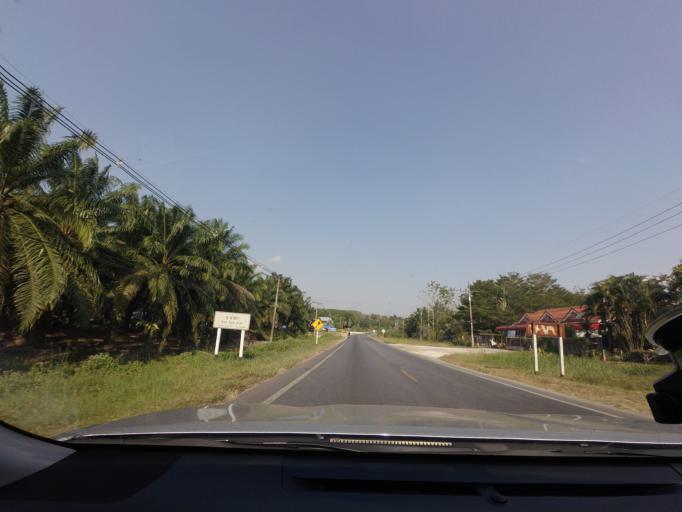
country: TH
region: Surat Thani
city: Phrasaeng
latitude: 8.5606
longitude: 99.1491
